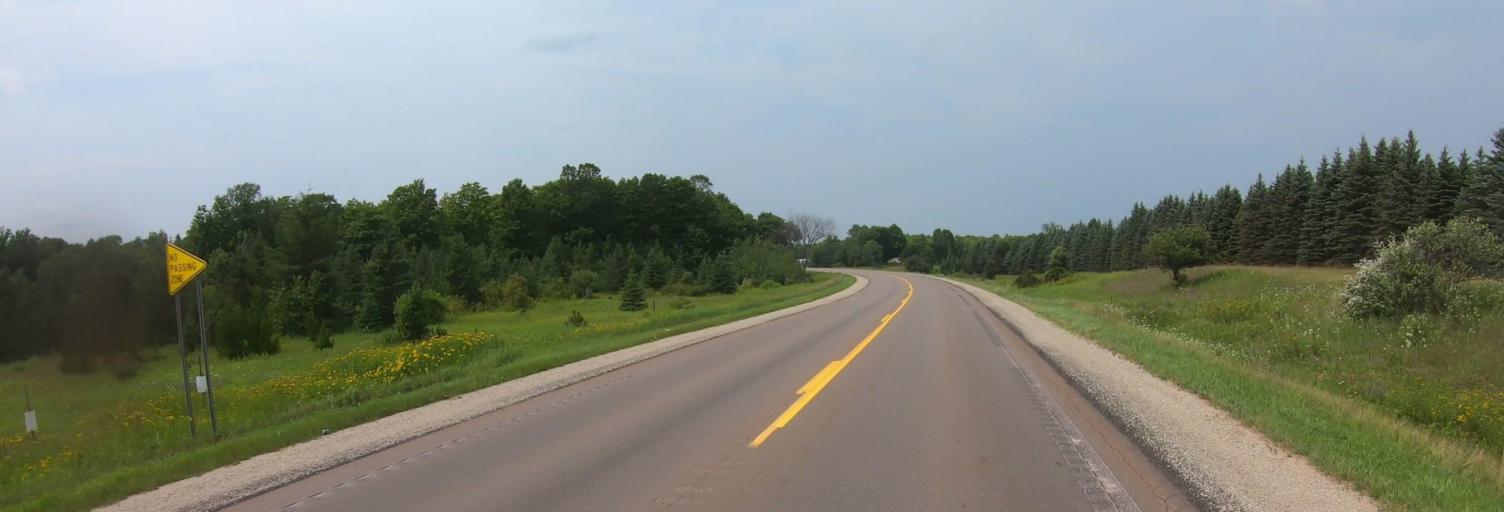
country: US
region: Michigan
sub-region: Alger County
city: Munising
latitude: 46.3445
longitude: -86.9532
